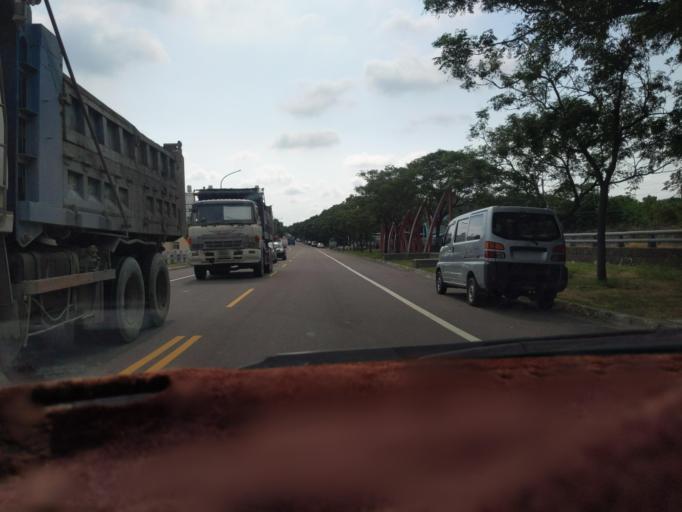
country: TW
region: Taiwan
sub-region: Yunlin
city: Douliu
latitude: 23.8048
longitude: 120.4590
